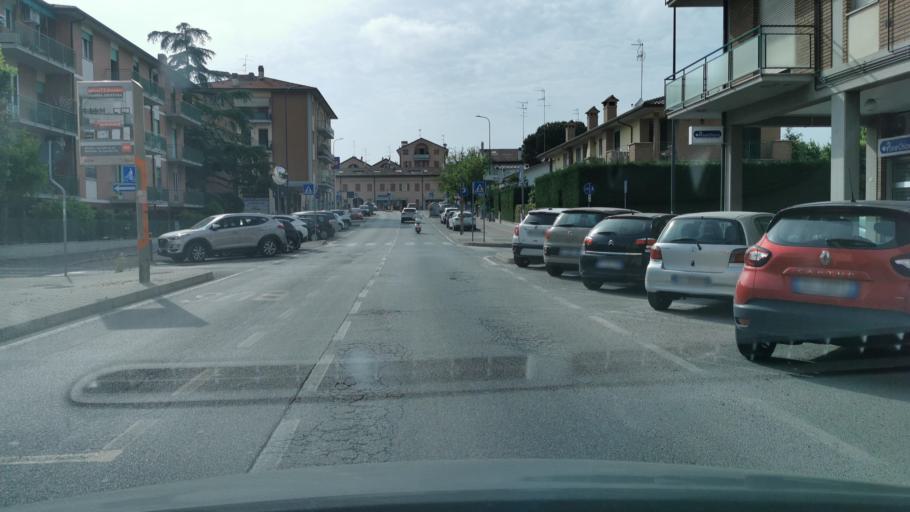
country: IT
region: Emilia-Romagna
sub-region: Provincia di Ravenna
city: Ravenna
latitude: 44.4059
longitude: 12.2006
